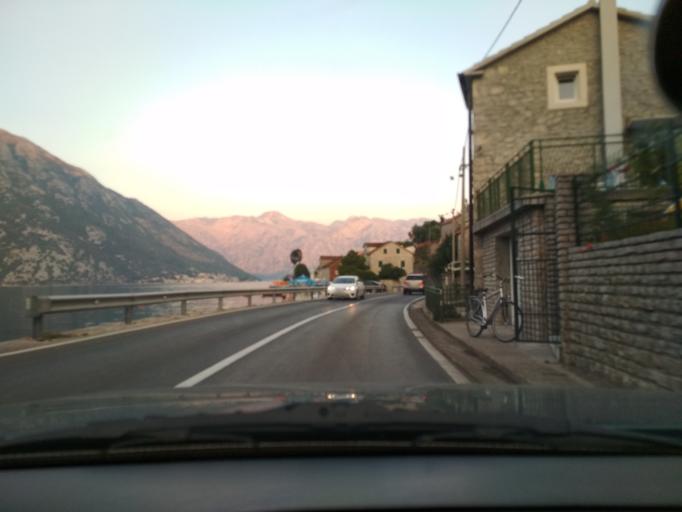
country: ME
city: Lipci
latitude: 42.4867
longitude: 18.6640
